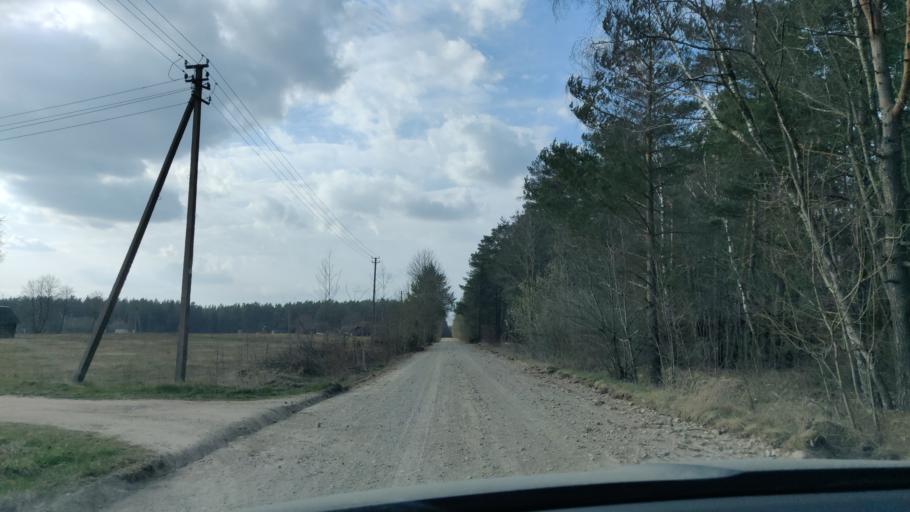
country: LT
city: Lentvaris
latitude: 54.5944
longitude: 25.0857
